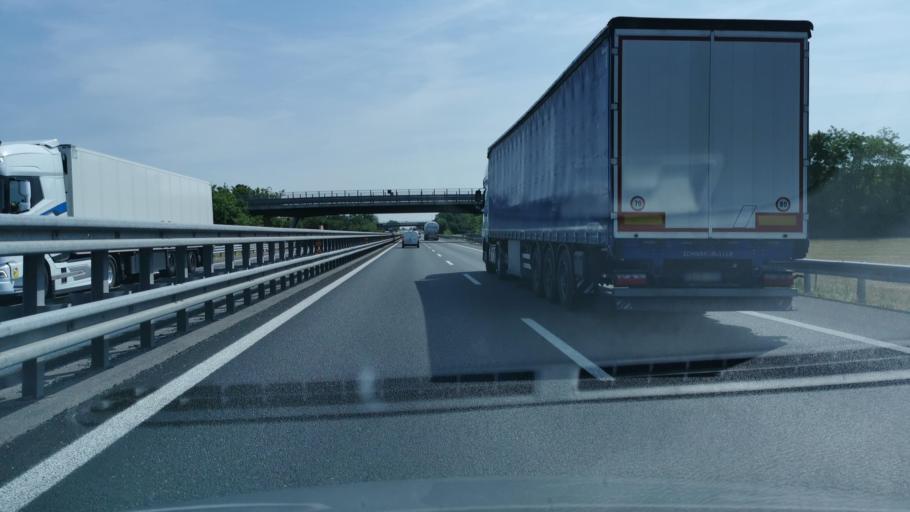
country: IT
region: Lombardy
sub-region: Provincia di Pavia
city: Robecco Pavese
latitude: 45.0444
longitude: 9.1535
